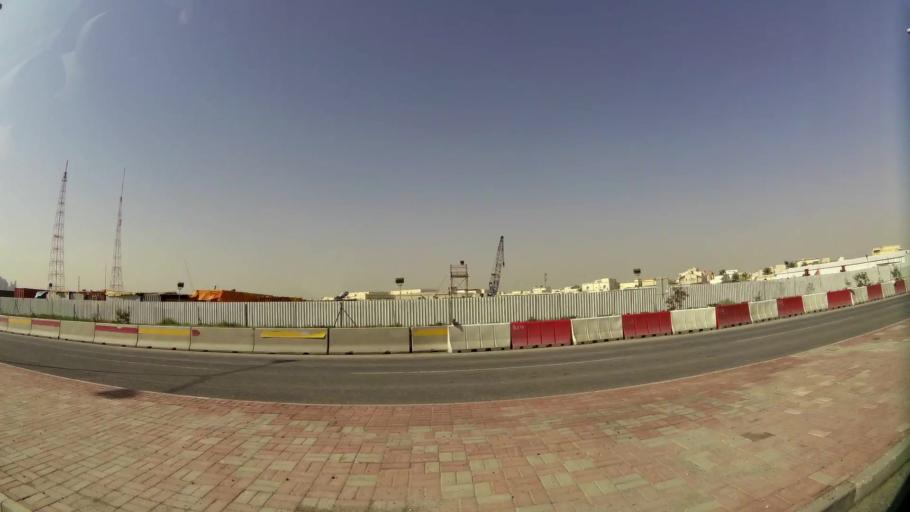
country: QA
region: Baladiyat ad Dawhah
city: Doha
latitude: 25.3395
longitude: 51.5131
